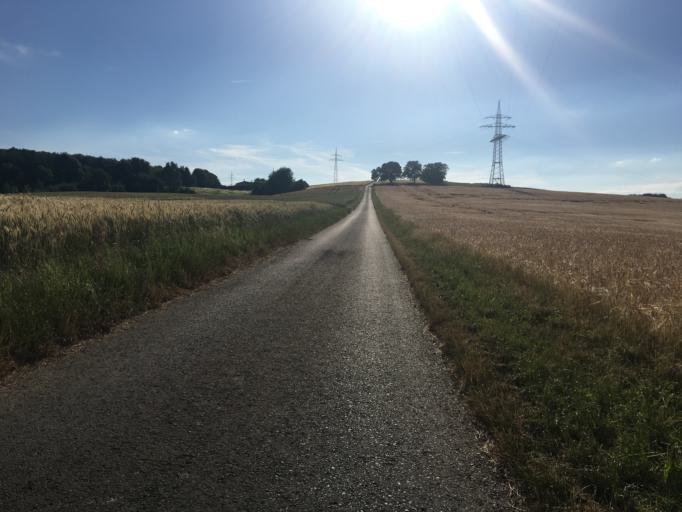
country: DE
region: Hesse
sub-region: Regierungsbezirk Darmstadt
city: Gelnhausen
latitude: 50.1811
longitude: 9.1849
